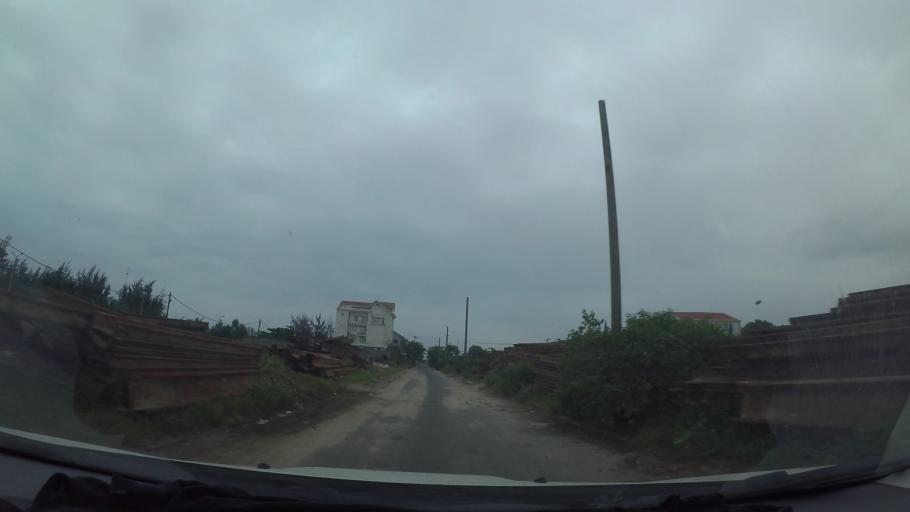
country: VN
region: Da Nang
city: Lien Chieu
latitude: 16.0889
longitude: 108.1529
